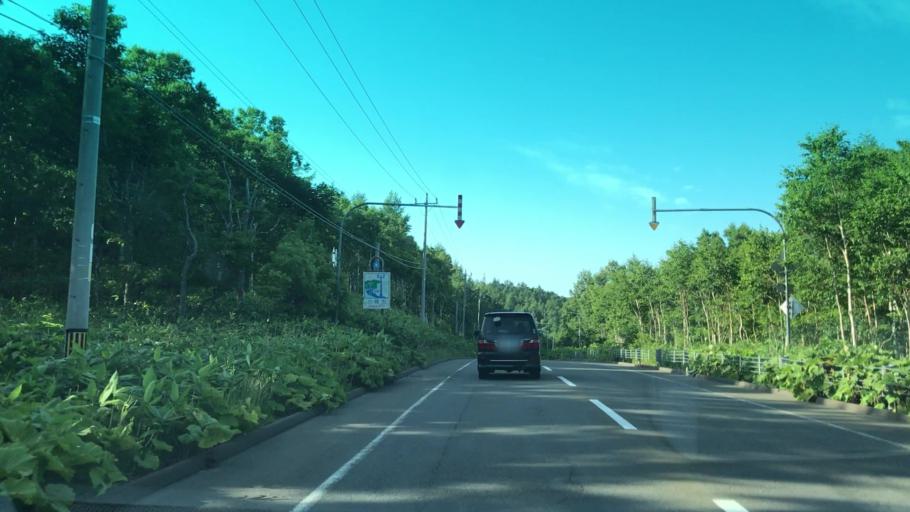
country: JP
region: Hokkaido
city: Otaru
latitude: 43.1056
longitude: 141.0049
